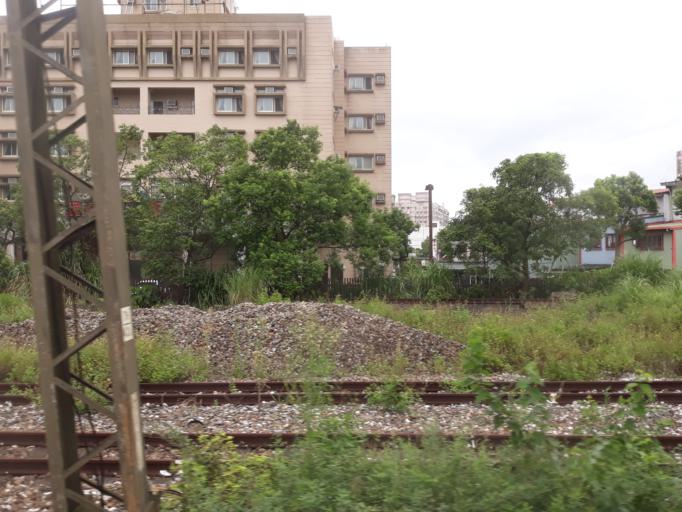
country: TW
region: Taiwan
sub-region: Yilan
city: Yilan
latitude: 24.6800
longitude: 121.7746
